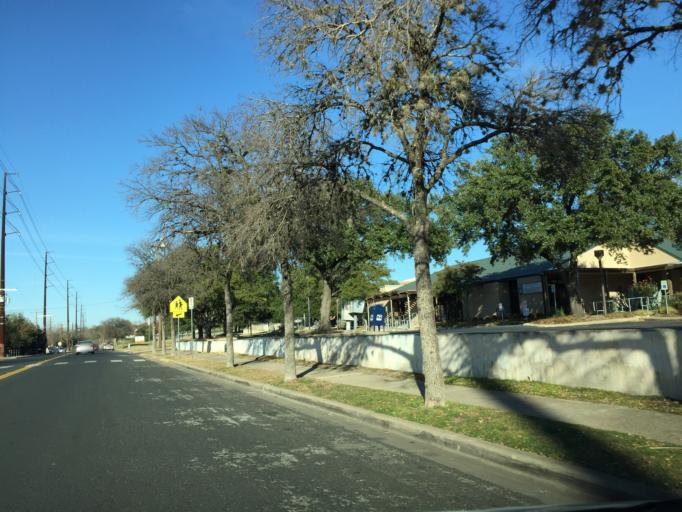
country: US
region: Texas
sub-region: Travis County
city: Austin
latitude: 30.2288
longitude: -97.7713
